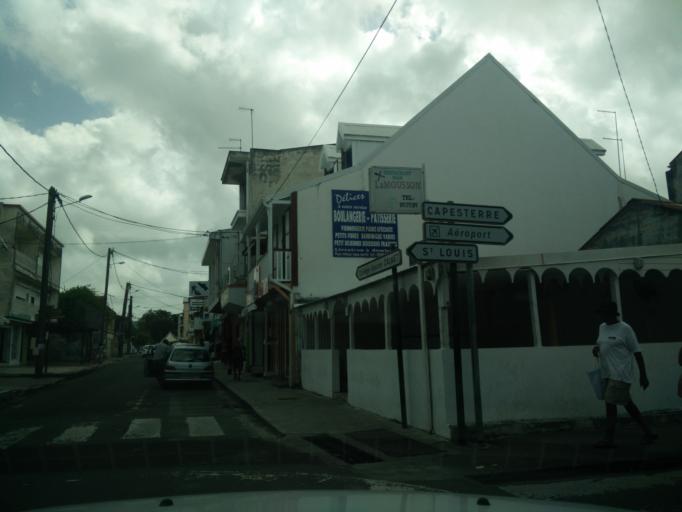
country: GP
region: Guadeloupe
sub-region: Guadeloupe
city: Grand-Bourg
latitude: 15.8829
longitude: -61.3160
